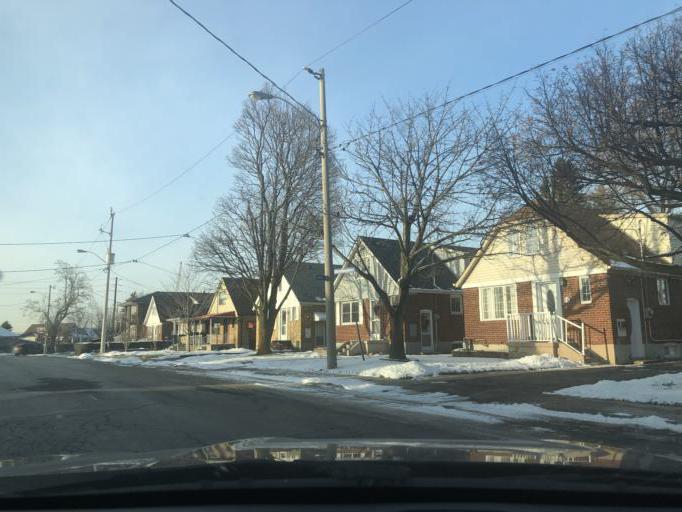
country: CA
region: Ontario
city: Toronto
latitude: 43.6951
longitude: -79.4685
